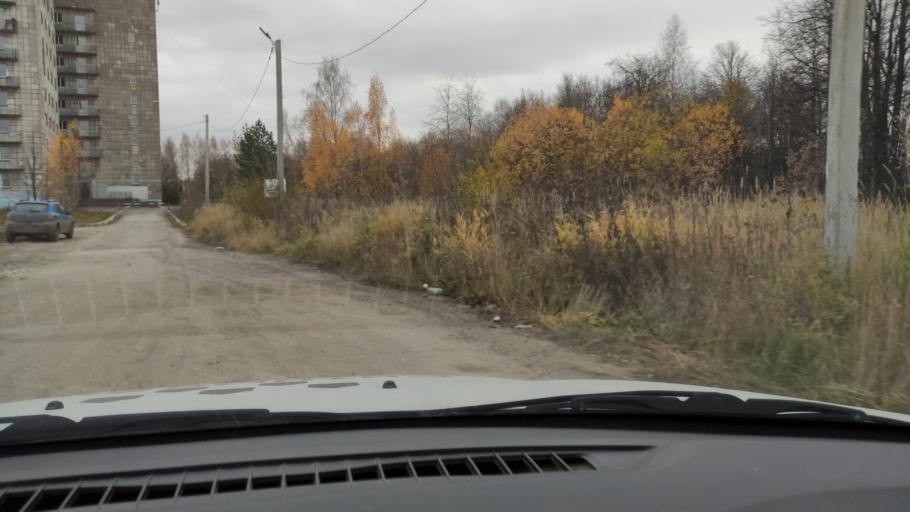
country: RU
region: Perm
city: Froly
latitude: 57.9561
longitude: 56.2738
